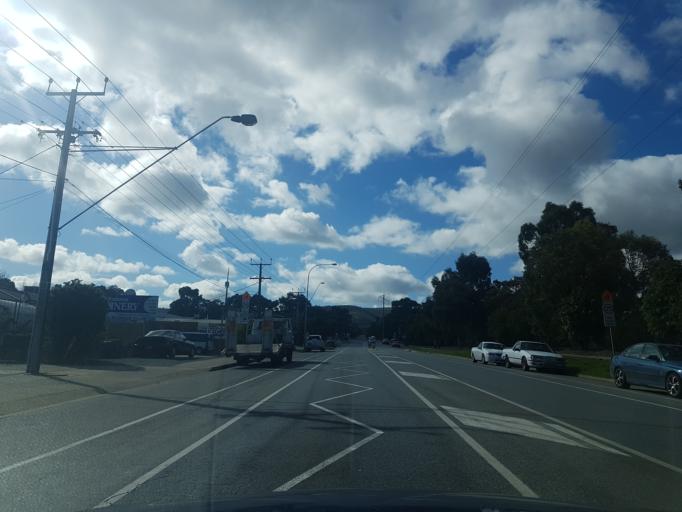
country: AU
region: South Australia
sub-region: Tea Tree Gully
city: Hope Valley
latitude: -34.8325
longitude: 138.7046
